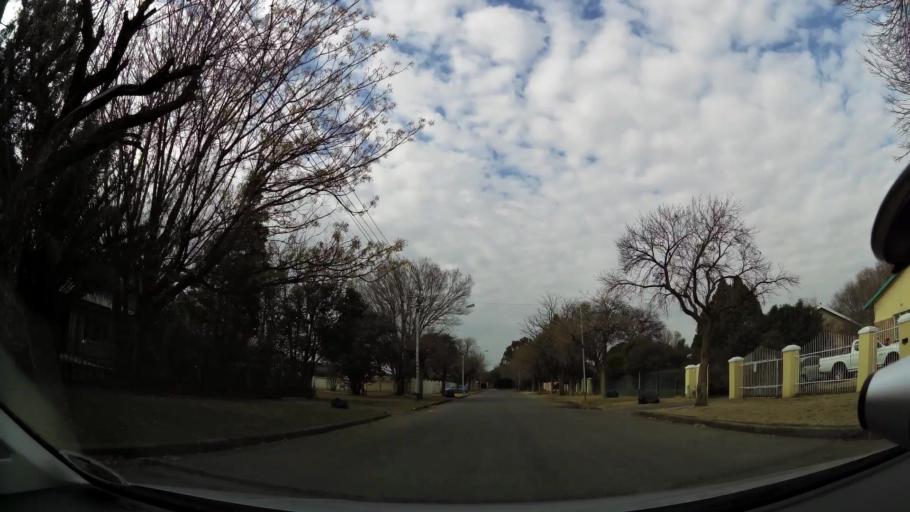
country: ZA
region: Orange Free State
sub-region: Mangaung Metropolitan Municipality
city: Bloemfontein
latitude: -29.0854
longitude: 26.2529
